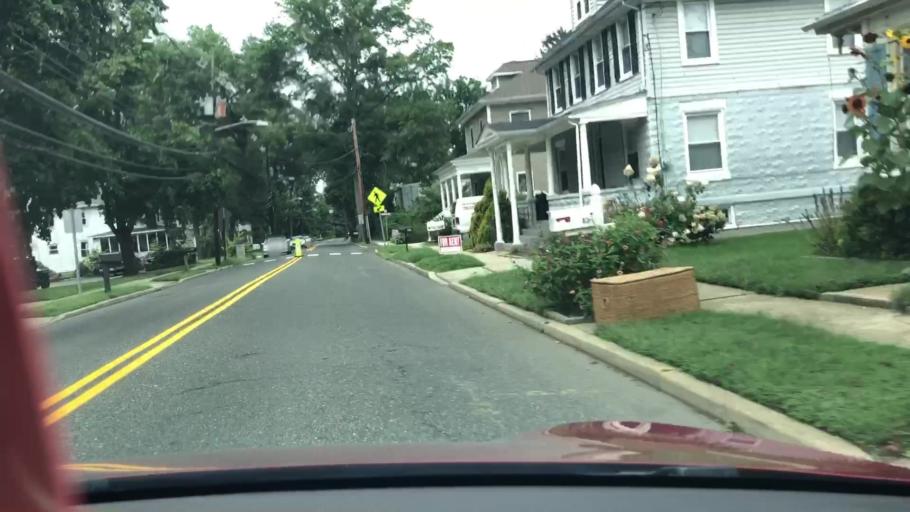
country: US
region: New Jersey
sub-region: Monmouth County
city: Allentown
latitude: 40.1799
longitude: -74.5874
